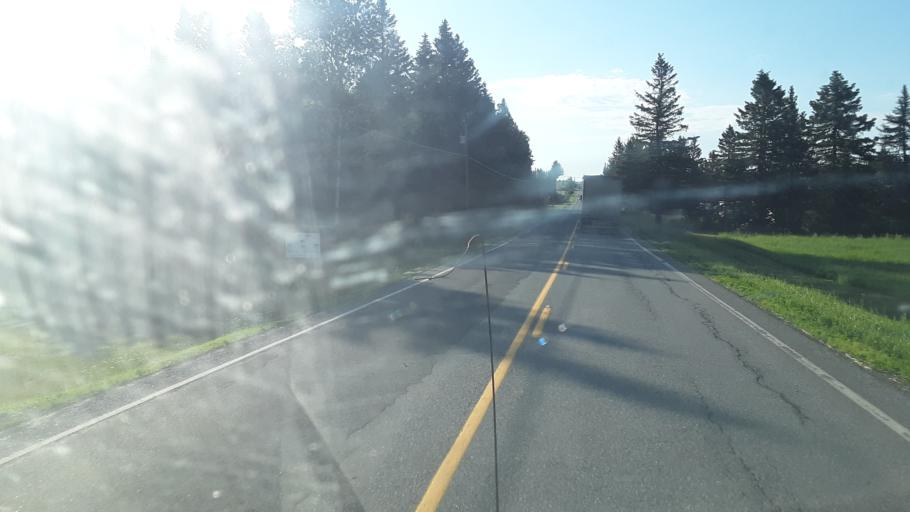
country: US
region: Maine
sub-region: Penobscot County
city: Patten
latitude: 46.1409
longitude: -68.2012
